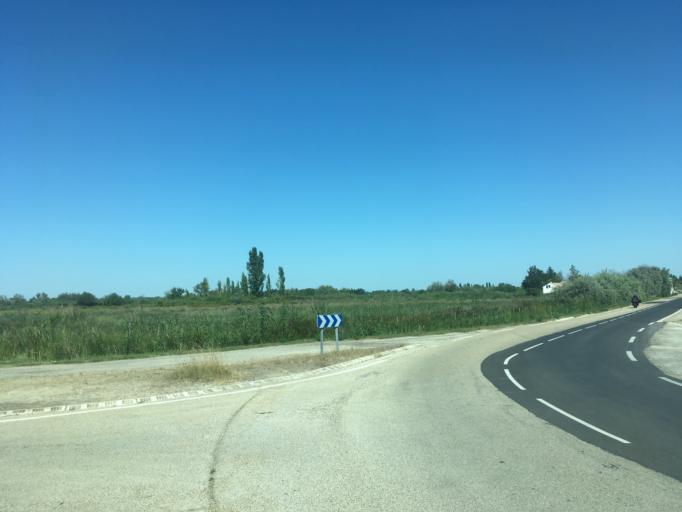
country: FR
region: Provence-Alpes-Cote d'Azur
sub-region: Departement des Bouches-du-Rhone
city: Saintes-Maries-de-la-Mer
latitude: 43.5223
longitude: 4.4023
